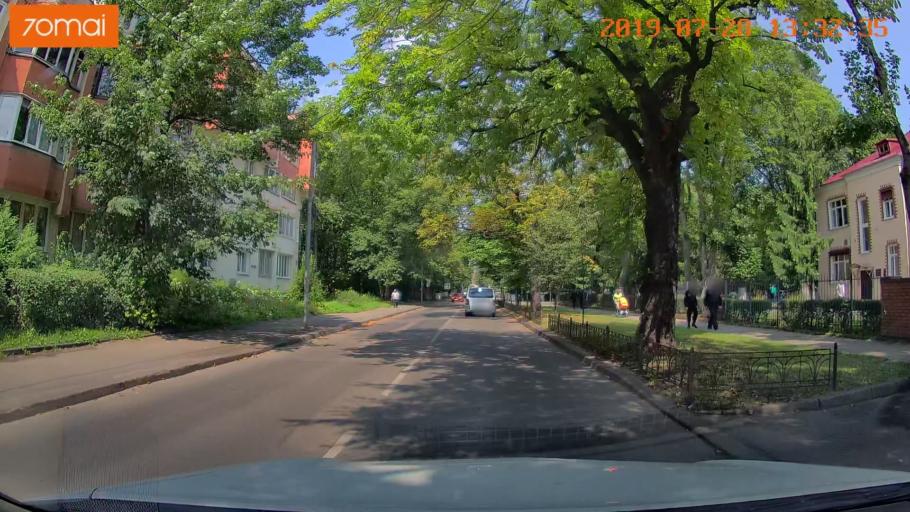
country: RU
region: Kaliningrad
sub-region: Gorod Kaliningrad
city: Kaliningrad
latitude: 54.7222
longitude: 20.4941
